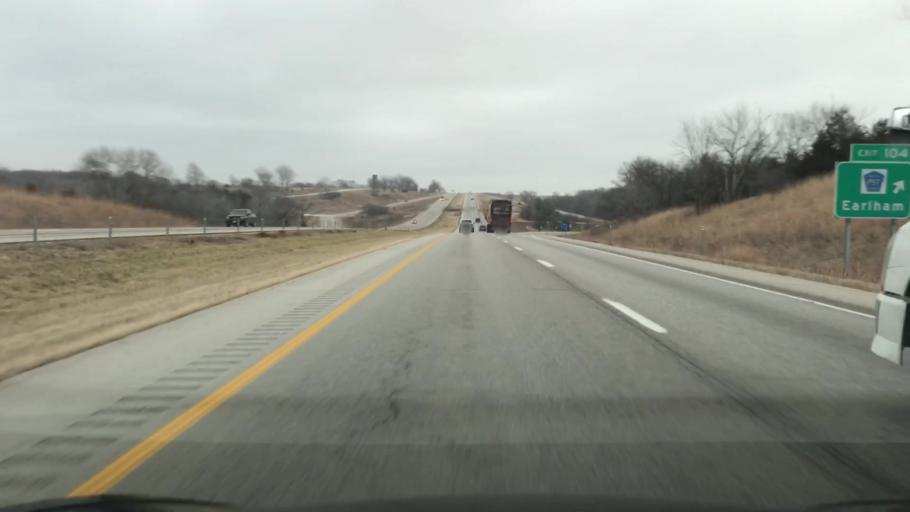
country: US
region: Iowa
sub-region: Madison County
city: Earlham
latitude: 41.5175
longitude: -94.1298
